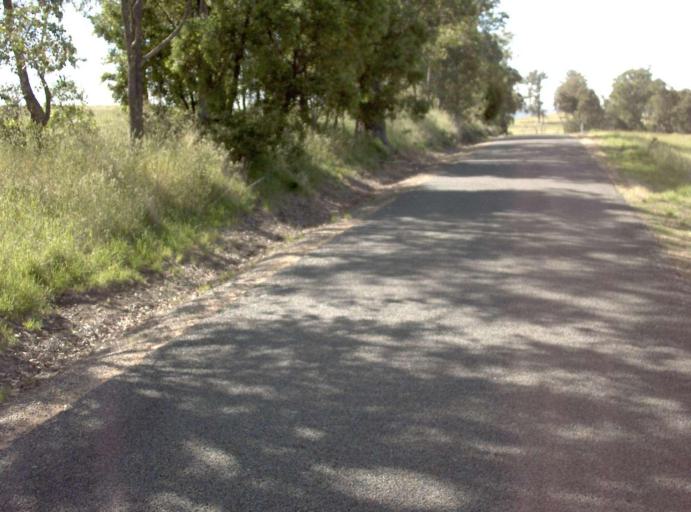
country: AU
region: Victoria
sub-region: East Gippsland
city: Lakes Entrance
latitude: -37.4831
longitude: 148.1270
